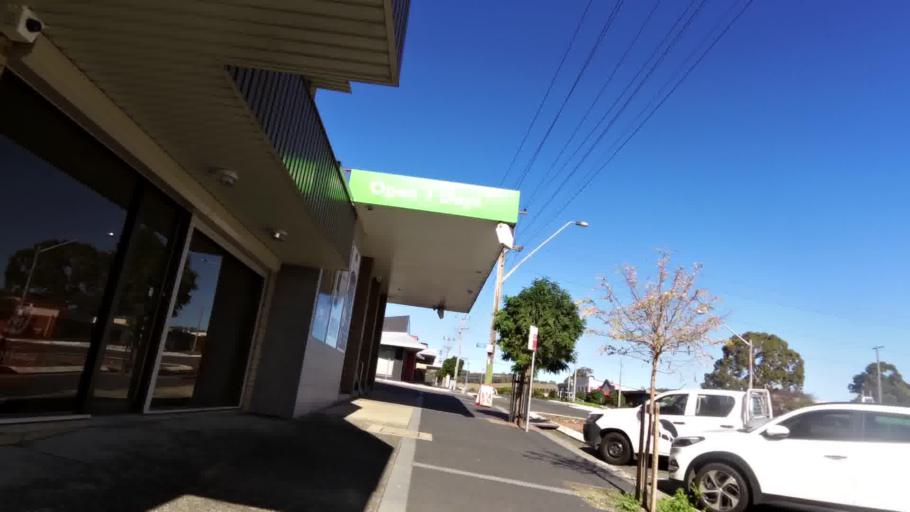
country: AU
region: New South Wales
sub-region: Shellharbour
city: Albion Park Rail
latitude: -34.5636
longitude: 150.8193
